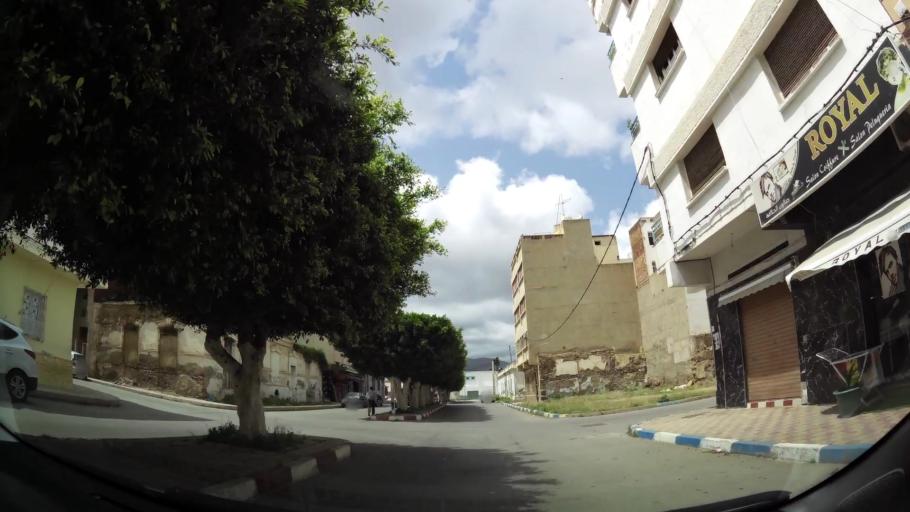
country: MA
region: Oriental
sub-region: Nador
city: Nador
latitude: 35.1822
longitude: -2.9263
